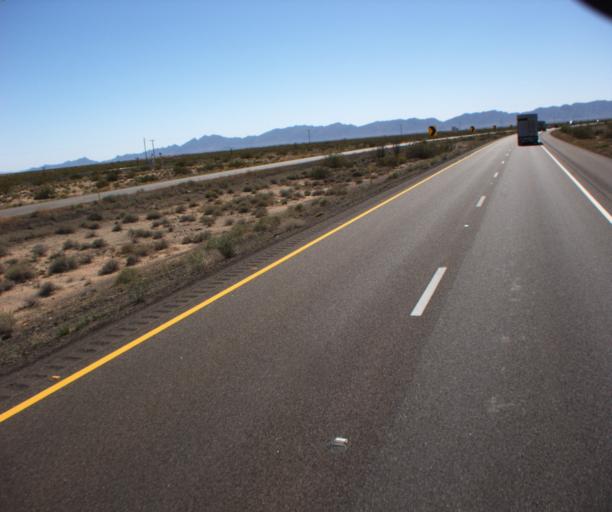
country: US
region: Arizona
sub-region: Yuma County
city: Wellton
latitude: 32.7923
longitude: -113.5556
